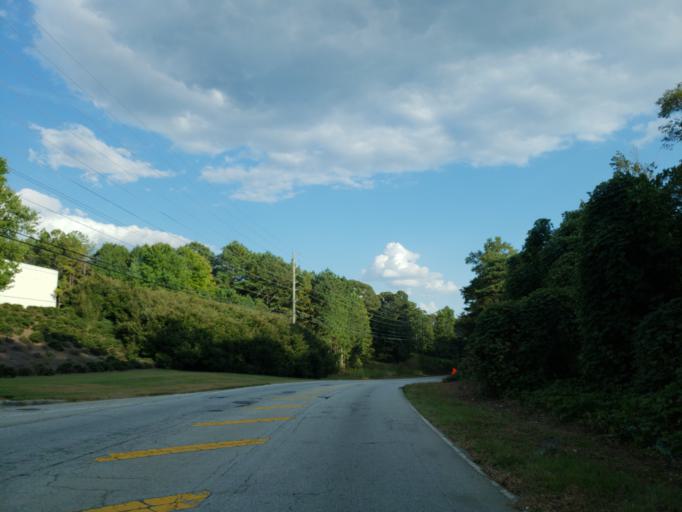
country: US
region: Georgia
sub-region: Cobb County
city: Mableton
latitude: 33.7548
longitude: -84.5842
